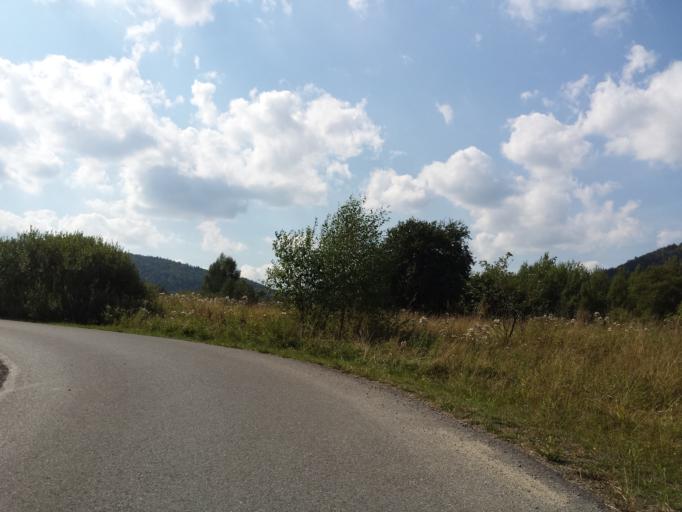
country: PL
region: Subcarpathian Voivodeship
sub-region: Powiat leski
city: Cisna
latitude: 49.1978
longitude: 22.3662
